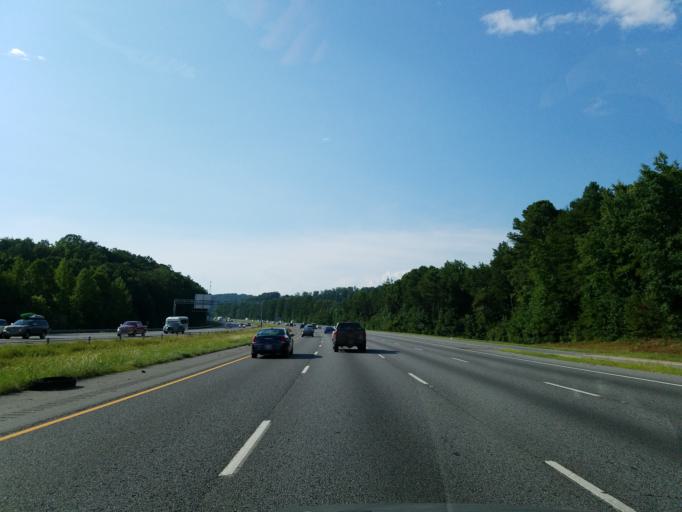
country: US
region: Georgia
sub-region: Bartow County
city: Cartersville
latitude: 34.1767
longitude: -84.7596
